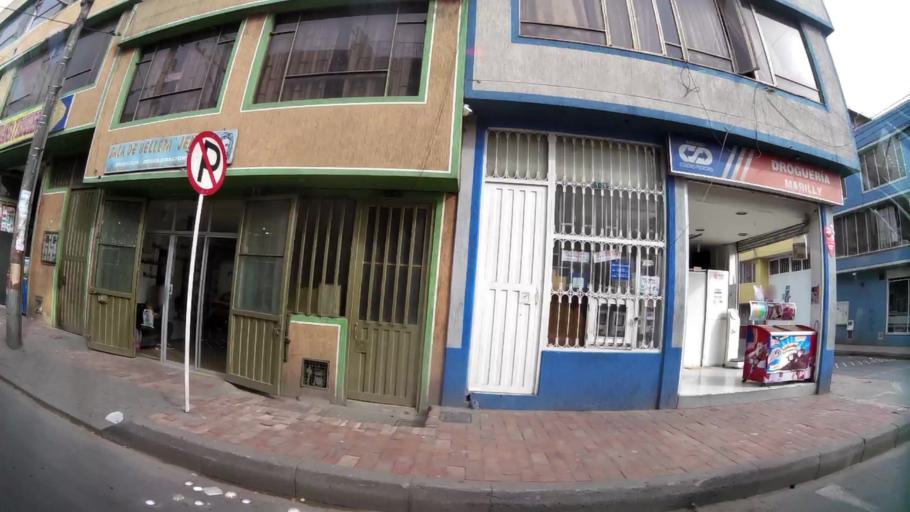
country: CO
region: Bogota D.C.
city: Bogota
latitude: 4.6367
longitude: -74.1574
